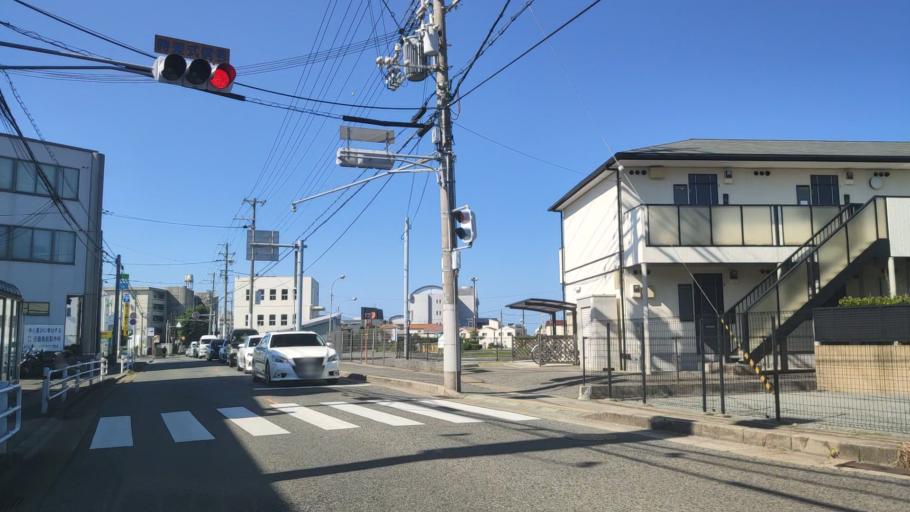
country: JP
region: Hyogo
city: Akashi
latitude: 34.6612
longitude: 135.0148
